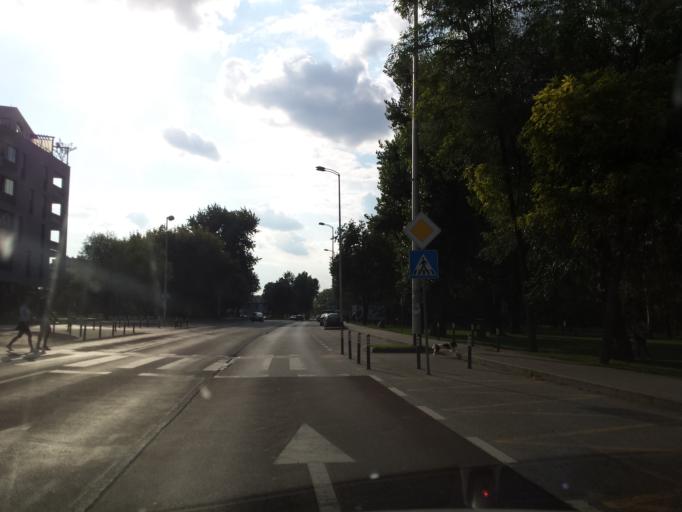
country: HR
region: Grad Zagreb
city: Novi Zagreb
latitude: 45.7829
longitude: 15.9868
